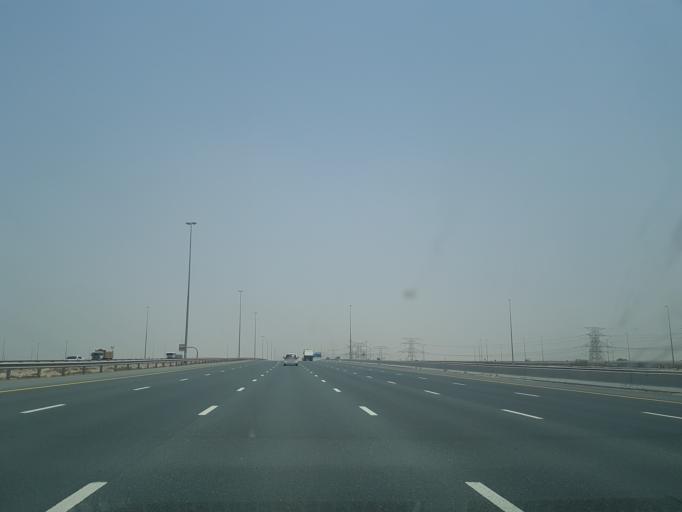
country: AE
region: Dubai
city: Dubai
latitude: 25.0849
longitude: 55.3891
